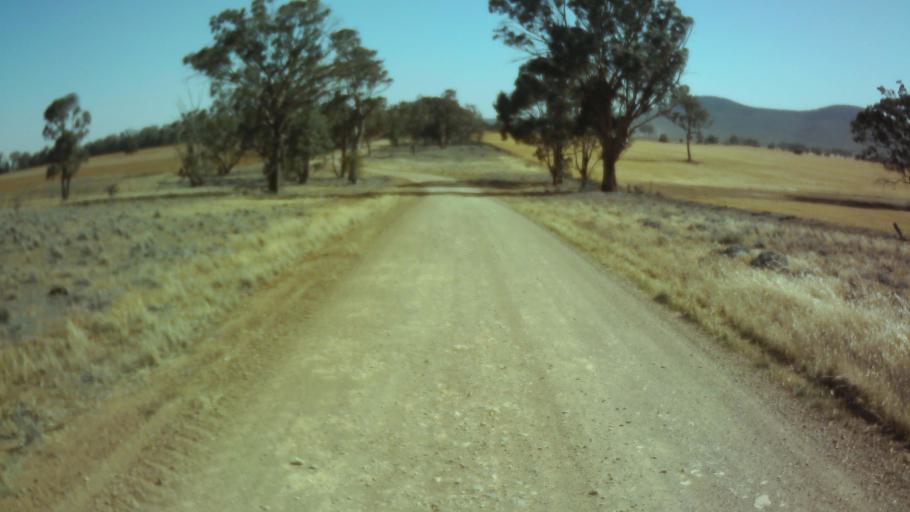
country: AU
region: New South Wales
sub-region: Weddin
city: Grenfell
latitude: -33.8551
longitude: 148.0157
